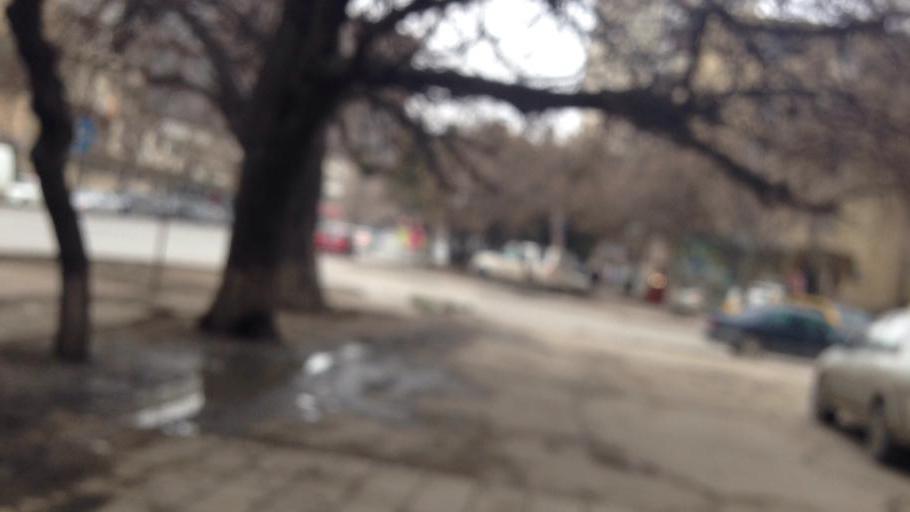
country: AZ
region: Baki
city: Badamdar
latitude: 40.3805
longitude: 49.8134
